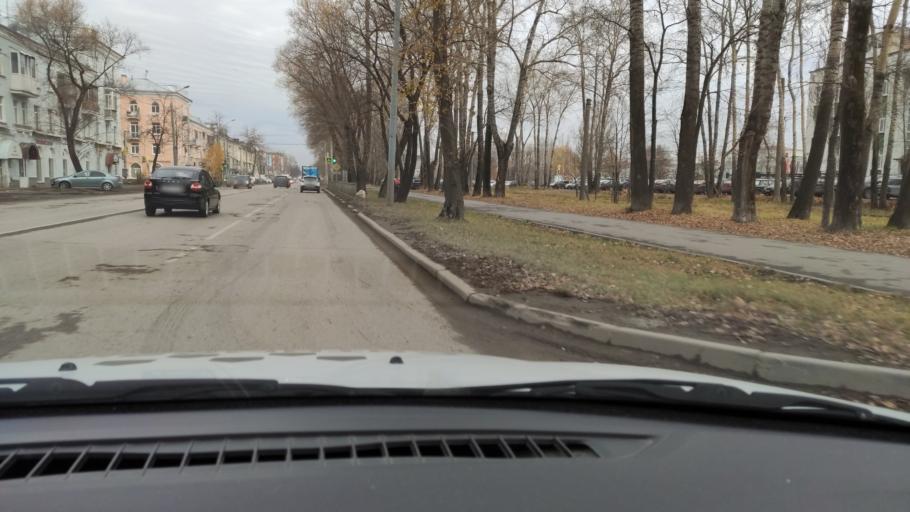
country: RU
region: Perm
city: Perm
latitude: 57.9618
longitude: 56.2437
